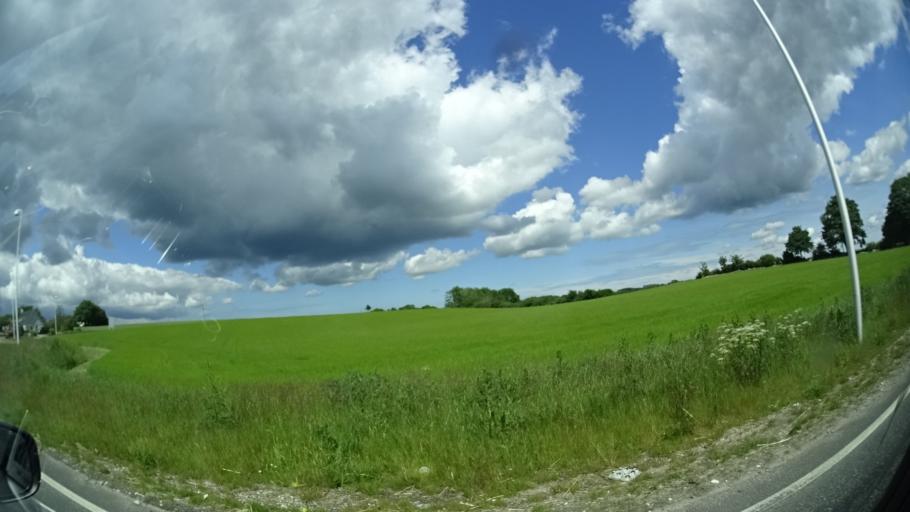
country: DK
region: Central Jutland
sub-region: Syddjurs Kommune
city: Ronde
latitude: 56.3162
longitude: 10.4252
